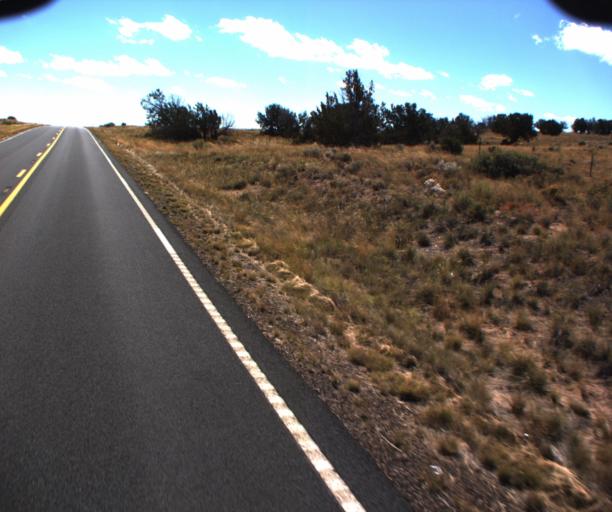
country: US
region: Arizona
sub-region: Apache County
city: Houck
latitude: 35.0237
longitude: -109.2447
